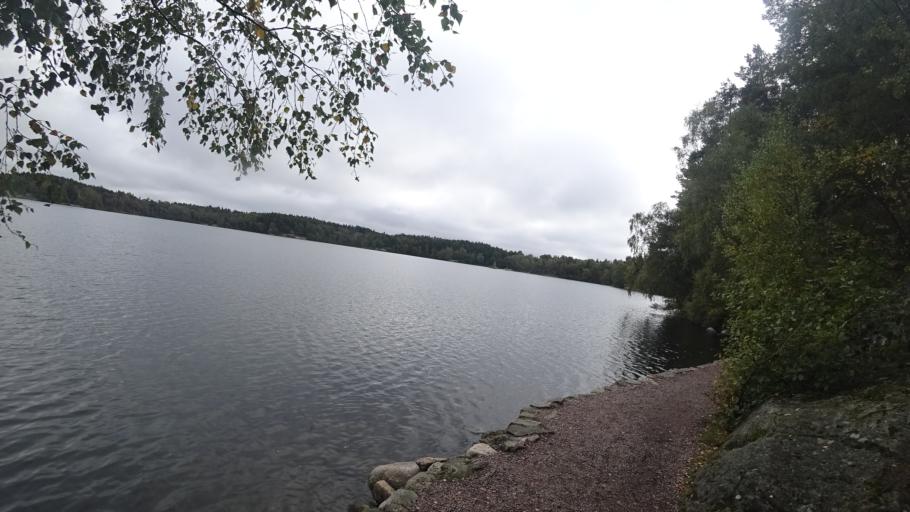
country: SE
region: Vaestra Goetaland
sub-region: Molndal
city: Moelndal
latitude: 57.6249
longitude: 11.9685
